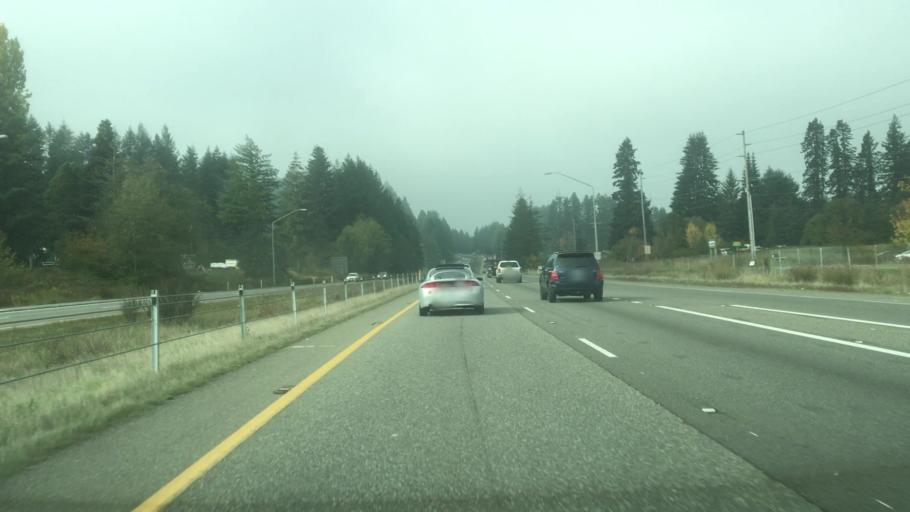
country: US
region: Washington
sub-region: Thurston County
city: Olympia
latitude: 47.0493
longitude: -122.9979
